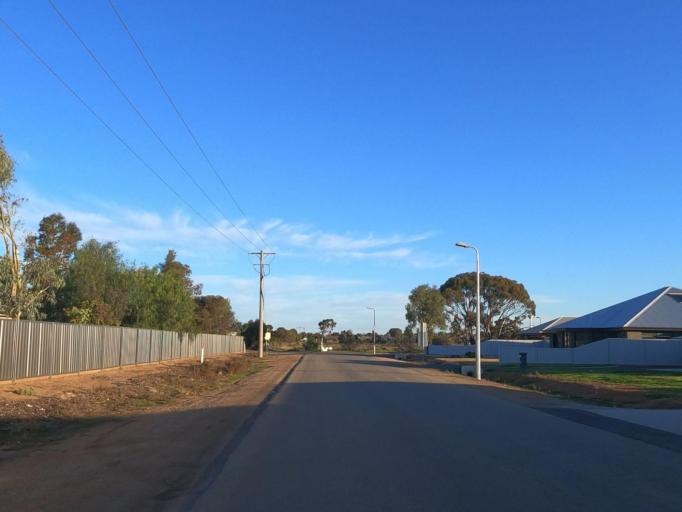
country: AU
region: Victoria
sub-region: Swan Hill
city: Swan Hill
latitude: -35.3321
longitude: 143.5343
